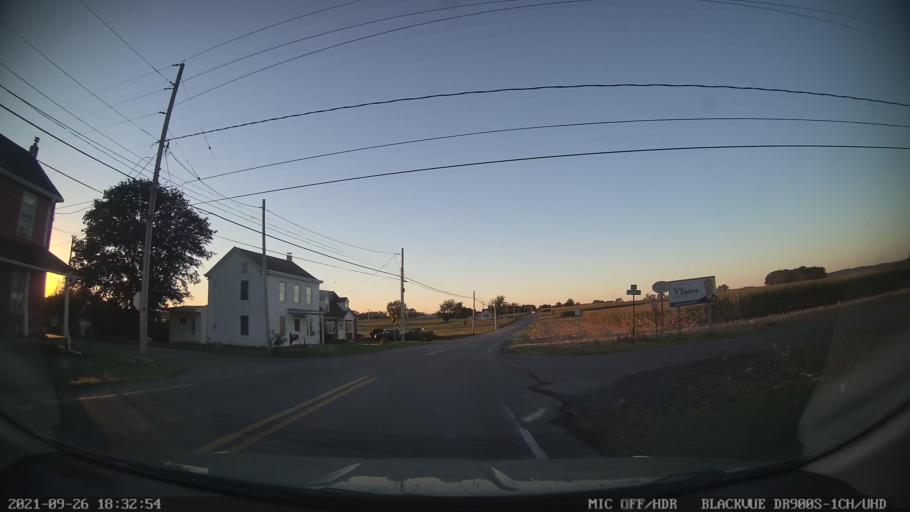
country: US
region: Pennsylvania
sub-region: Berks County
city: Kutztown
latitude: 40.4950
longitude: -75.7635
